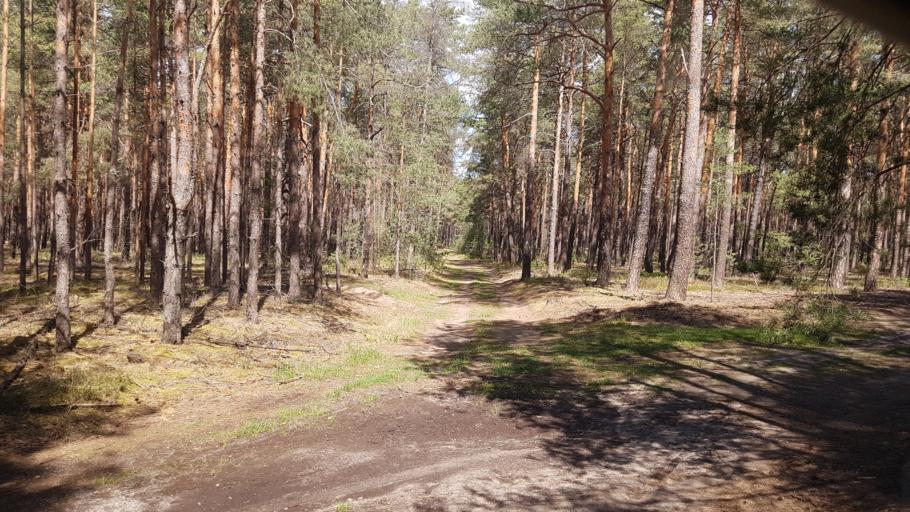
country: DE
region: Brandenburg
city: Sonnewalde
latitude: 51.6467
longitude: 13.6590
